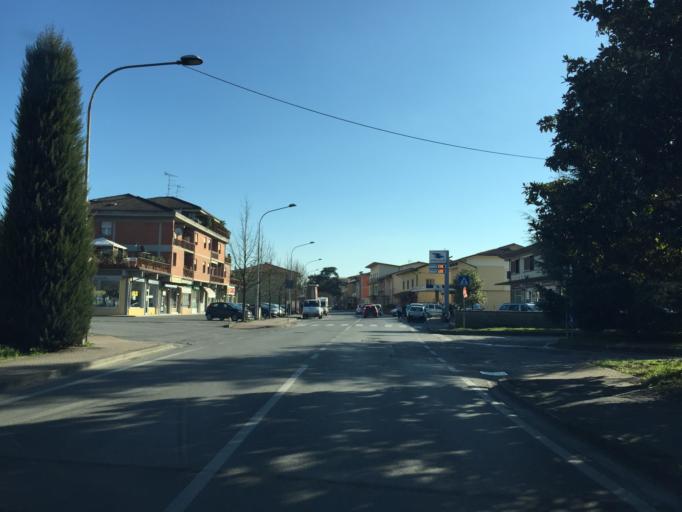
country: IT
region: Tuscany
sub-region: Provincia di Pistoia
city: Ponte Buggianese
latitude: 43.8453
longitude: 10.7471
